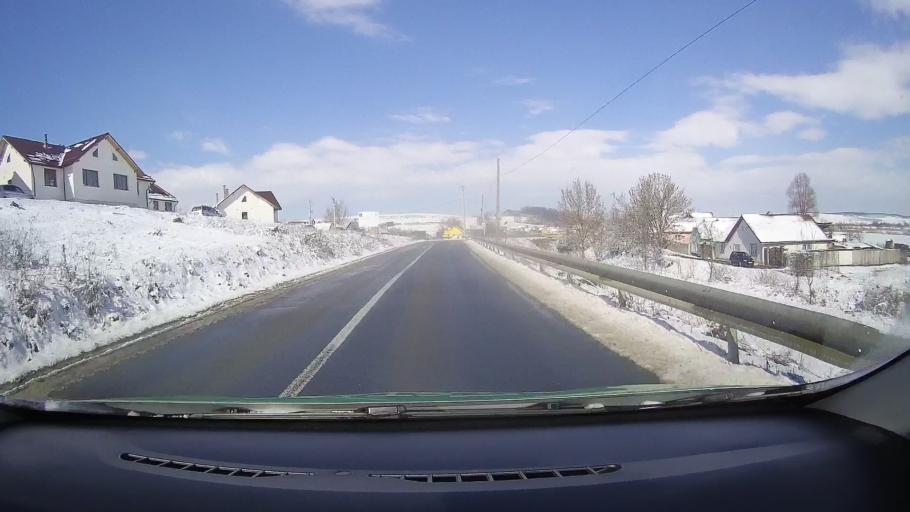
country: RO
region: Sibiu
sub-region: Comuna Nocrich
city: Nocrich
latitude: 45.8846
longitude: 24.4512
